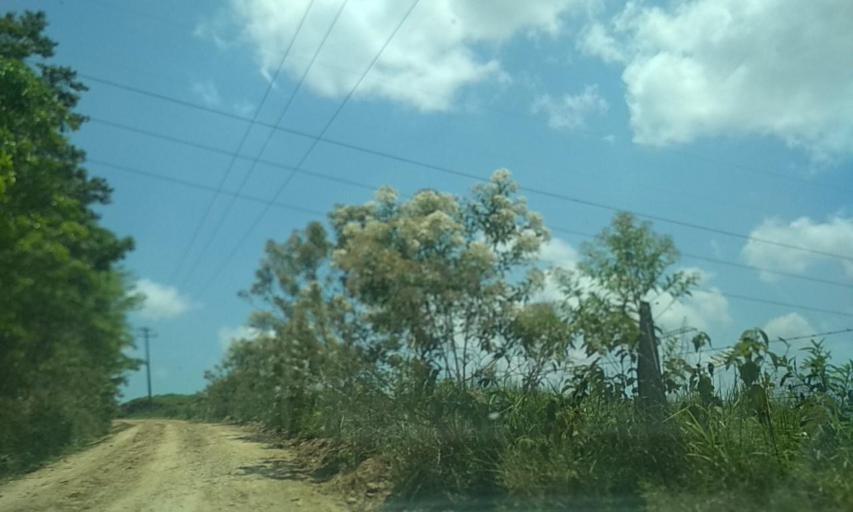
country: MX
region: Chiapas
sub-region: Tecpatan
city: Raudales Malpaso
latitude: 17.3983
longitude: -93.7481
